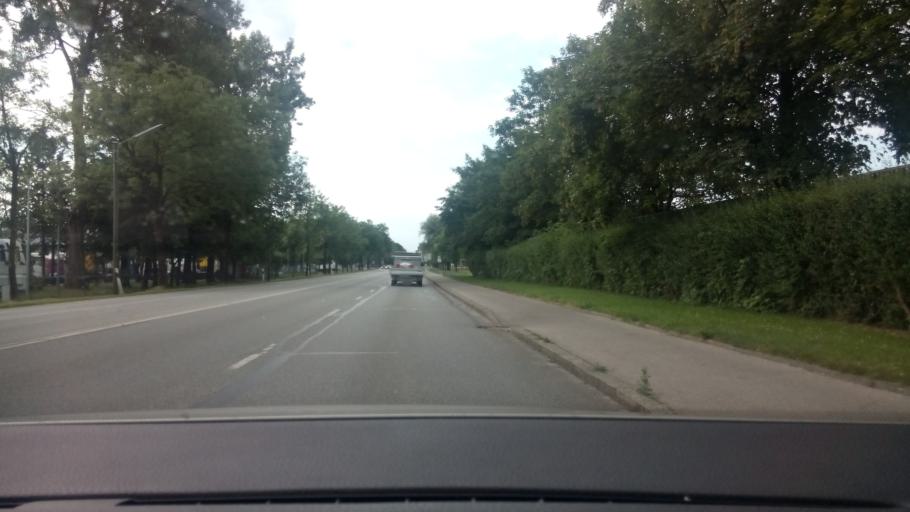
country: DE
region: Bavaria
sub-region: Upper Bavaria
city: Karlsfeld
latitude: 48.2195
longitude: 11.4773
